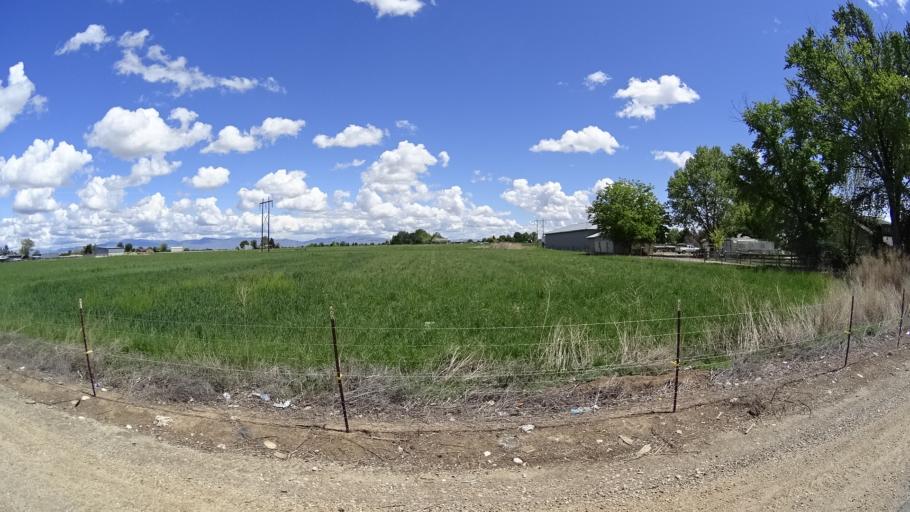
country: US
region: Idaho
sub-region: Ada County
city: Kuna
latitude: 43.5576
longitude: -116.4338
